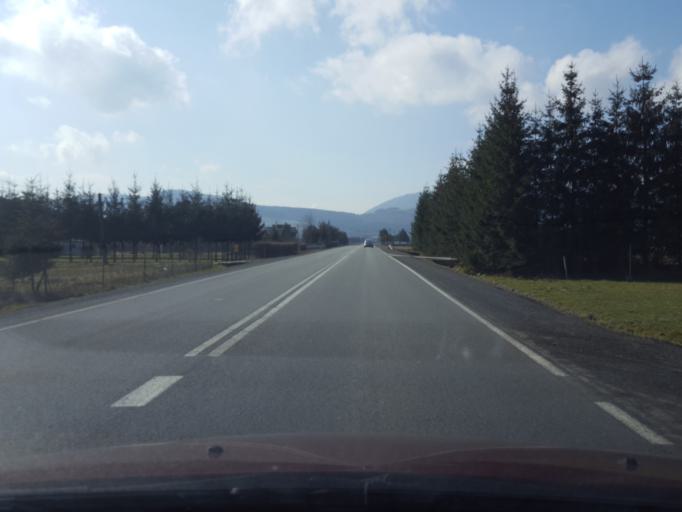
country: PL
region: Lesser Poland Voivodeship
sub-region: Powiat nowosadecki
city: Lososina Dolna
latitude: 49.7530
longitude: 20.6343
